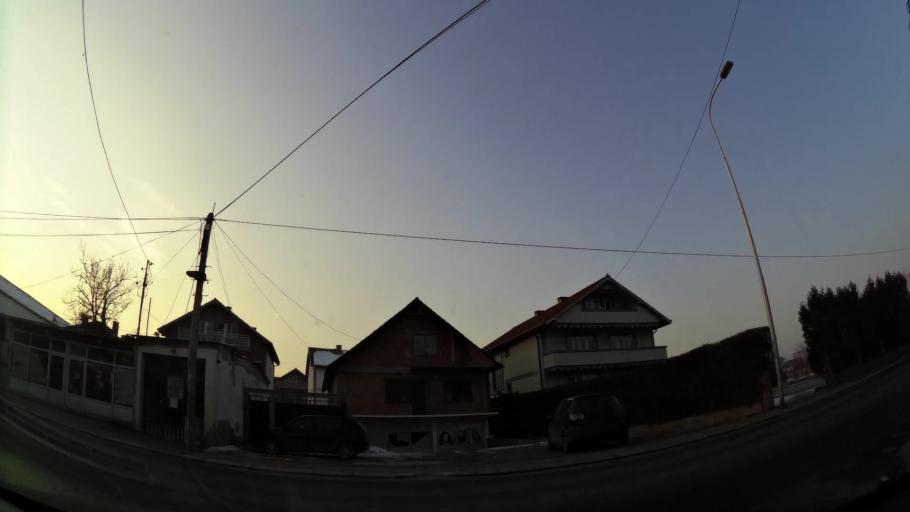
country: MK
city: Creshevo
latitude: 42.0147
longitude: 21.5112
